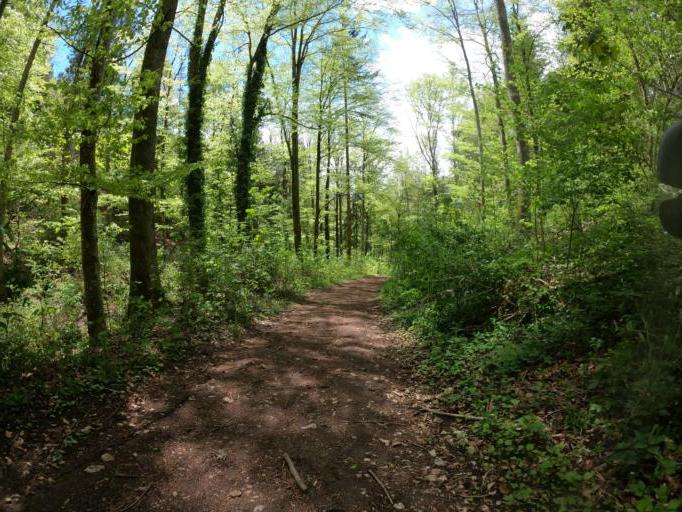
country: DE
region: Baden-Wuerttemberg
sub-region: Karlsruhe Region
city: Nagold
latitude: 48.5585
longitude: 8.7366
